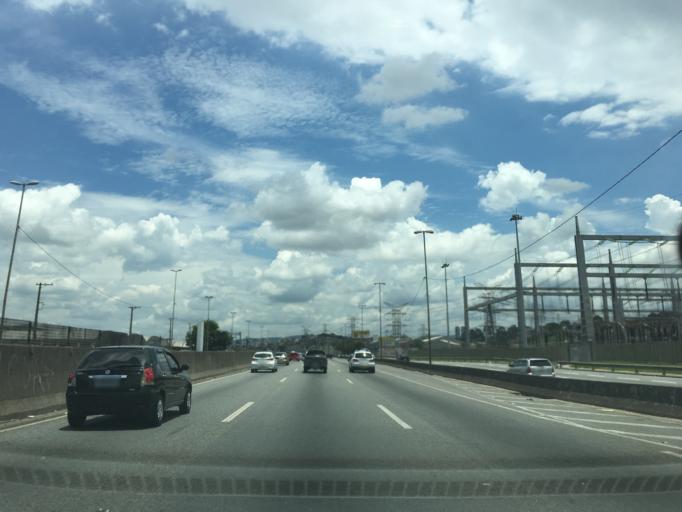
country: BR
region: Sao Paulo
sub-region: Guarulhos
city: Guarulhos
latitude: -23.4834
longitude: -46.5598
